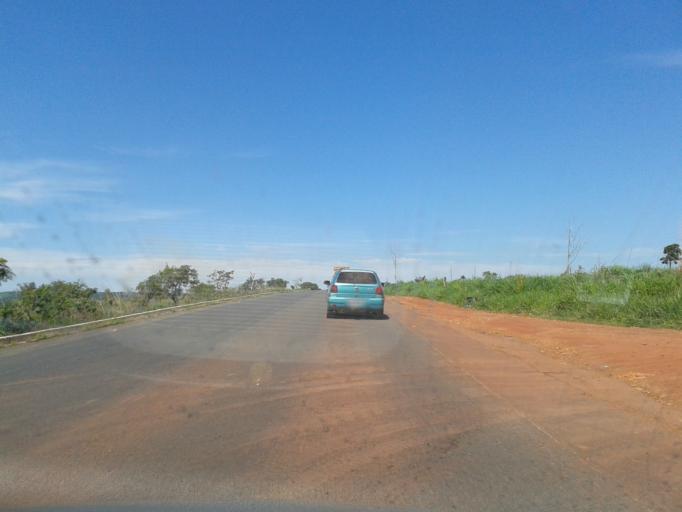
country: BR
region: Goias
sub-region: Bela Vista De Goias
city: Bela Vista de Goias
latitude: -17.1692
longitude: -48.7347
